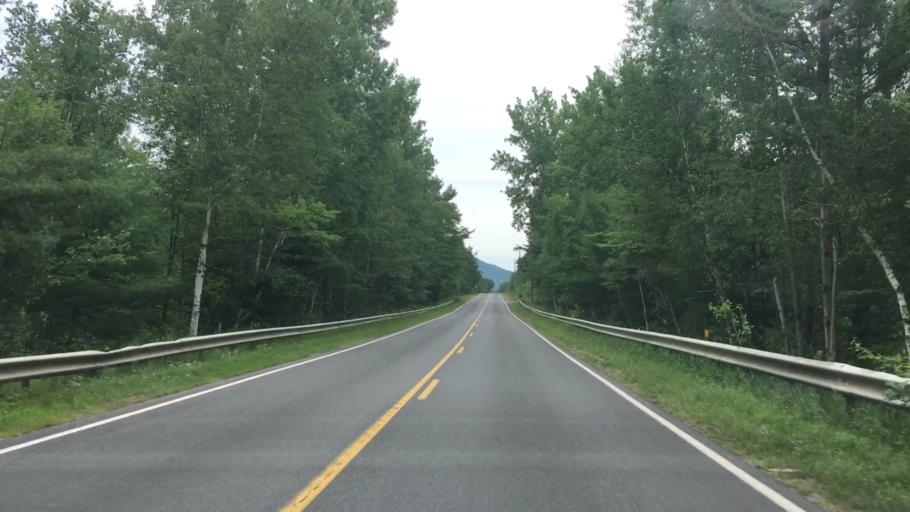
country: US
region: New York
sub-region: Essex County
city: Keeseville
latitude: 44.4726
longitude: -73.5939
